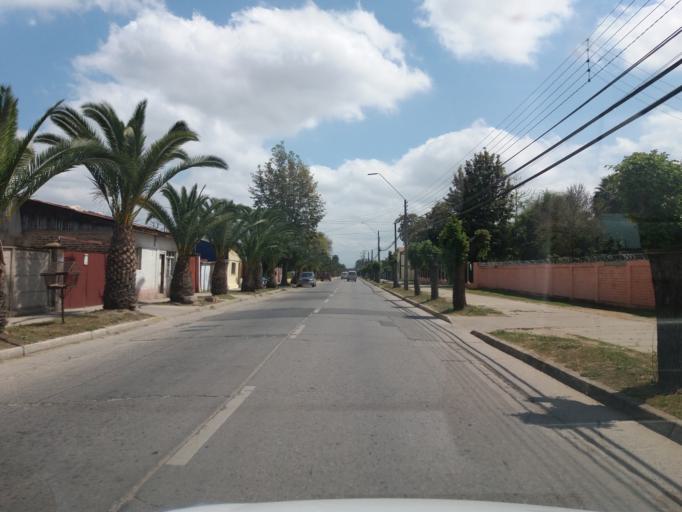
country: CL
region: Valparaiso
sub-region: Provincia de Marga Marga
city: Limache
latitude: -33.0079
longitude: -71.2515
